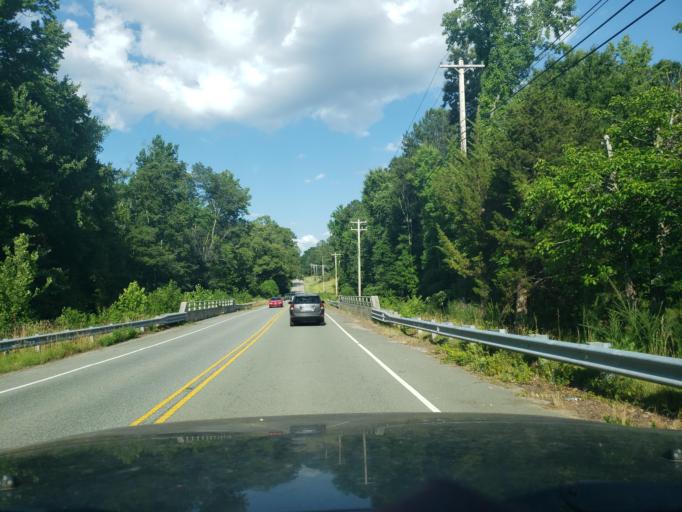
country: US
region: North Carolina
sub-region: Durham County
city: Durham
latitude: 35.9752
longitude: -78.9850
